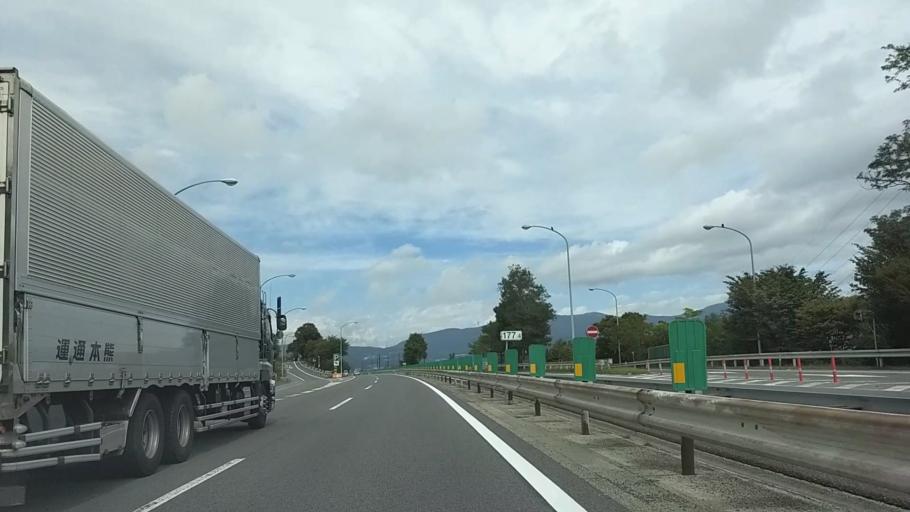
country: JP
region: Nagano
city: Suwa
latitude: 36.0235
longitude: 138.0796
